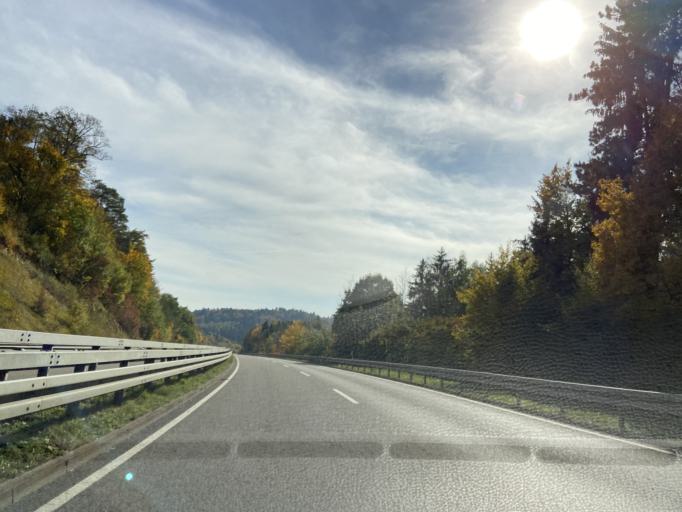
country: DE
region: Baden-Wuerttemberg
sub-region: Tuebingen Region
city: Sigmaringen
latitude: 48.1039
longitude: 9.2047
